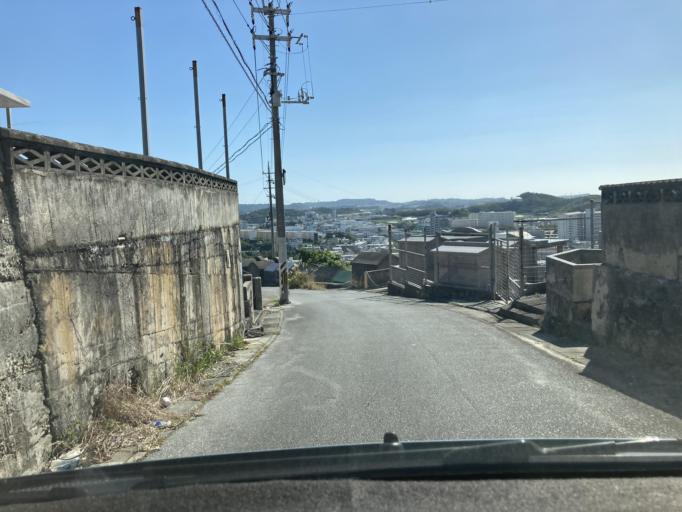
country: JP
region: Okinawa
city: Naha-shi
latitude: 26.2032
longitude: 127.7134
